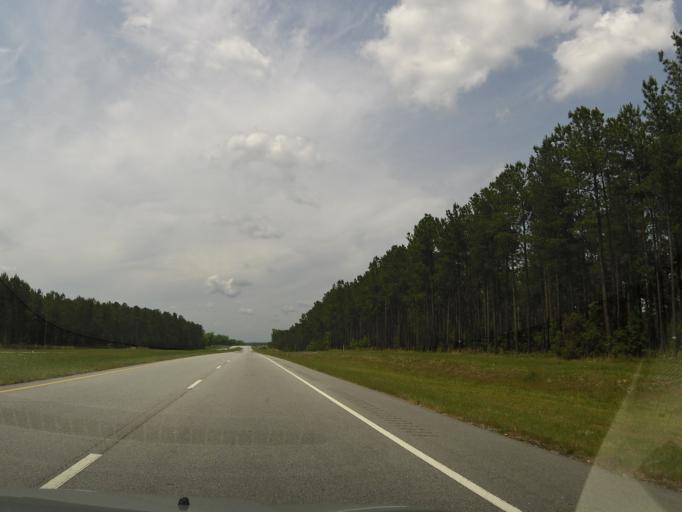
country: US
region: Georgia
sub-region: Jefferson County
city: Wadley
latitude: 32.7899
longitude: -82.3959
